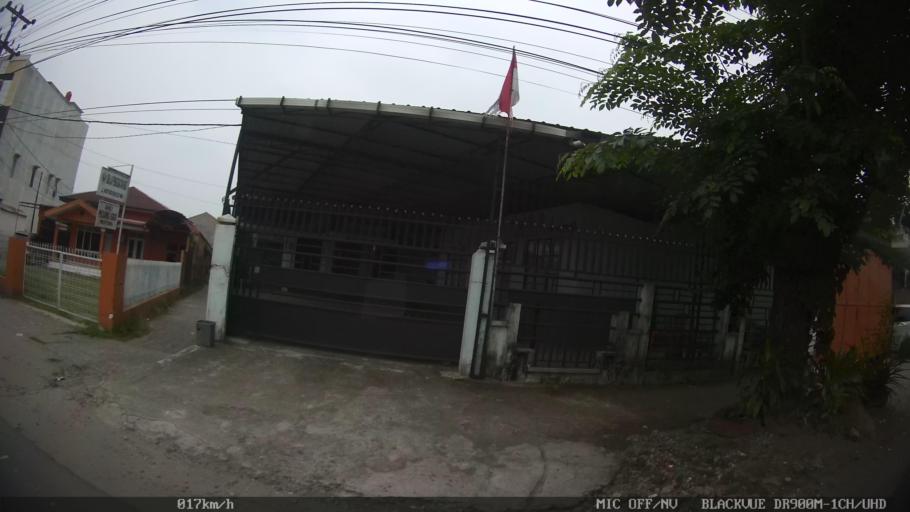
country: ID
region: North Sumatra
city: Medan
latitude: 3.5672
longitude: 98.7236
